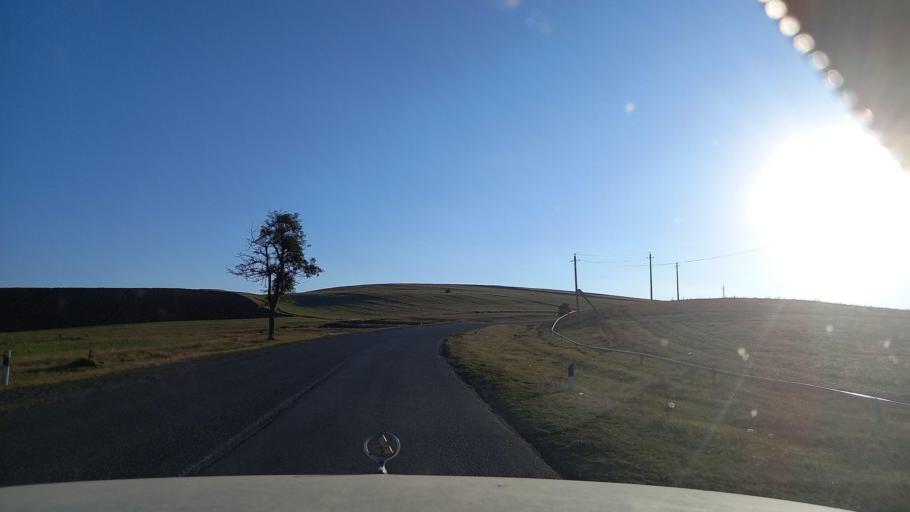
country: AZ
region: Shamkir Rayon
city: Shamkhor
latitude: 40.7669
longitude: 45.9527
